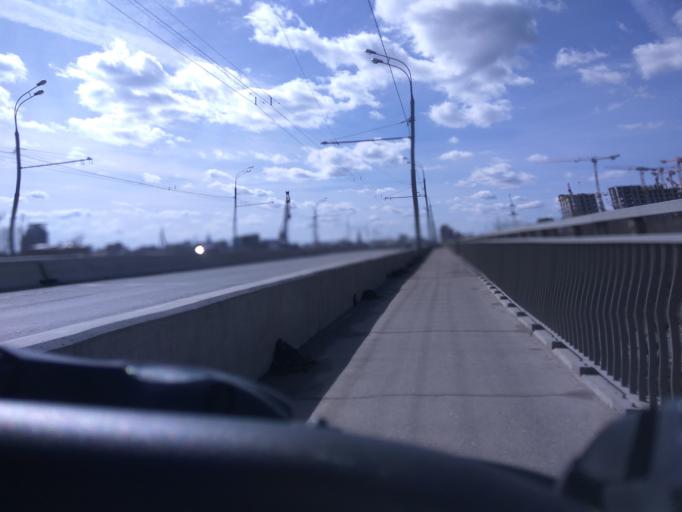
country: RU
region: Moskovskaya
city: Presnenskiy
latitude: 55.7546
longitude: 37.5204
